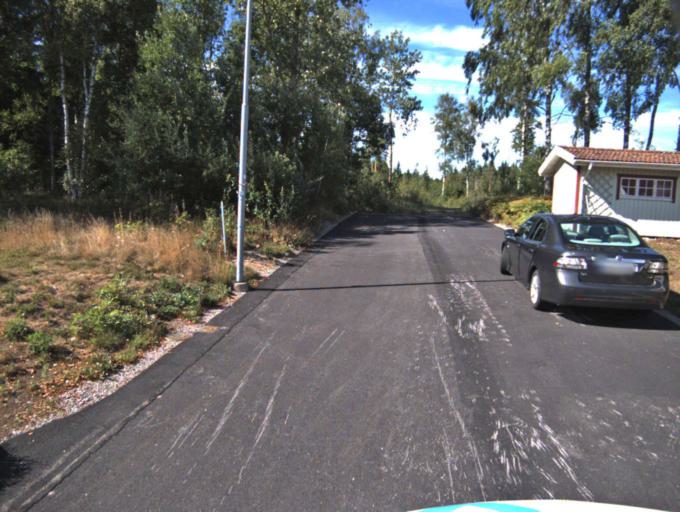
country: SE
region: Vaestra Goetaland
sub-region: Ulricehamns Kommun
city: Ulricehamn
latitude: 57.6969
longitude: 13.5693
